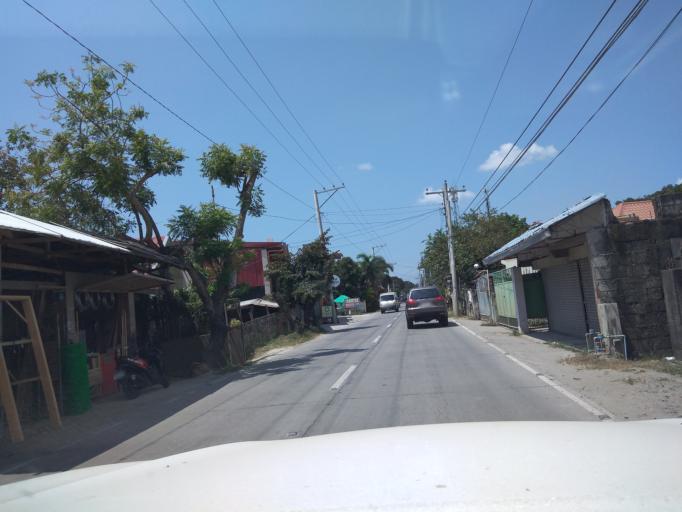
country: PH
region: Central Luzon
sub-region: Province of Pampanga
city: Lourdes
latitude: 15.0190
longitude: 120.8559
